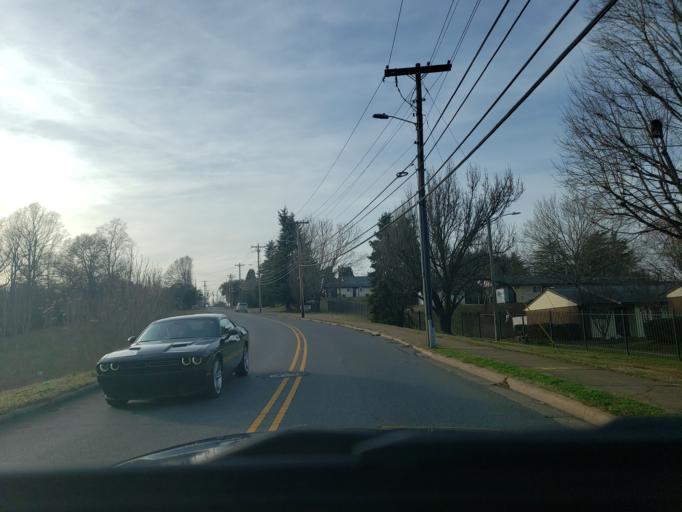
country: US
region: North Carolina
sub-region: Cleveland County
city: Shelby
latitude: 35.2894
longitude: -81.5322
